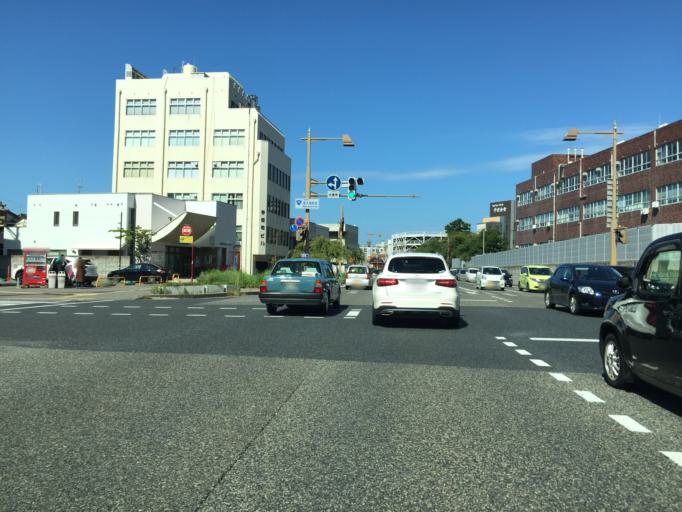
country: JP
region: Niigata
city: Niigata-shi
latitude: 37.9168
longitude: 139.0366
